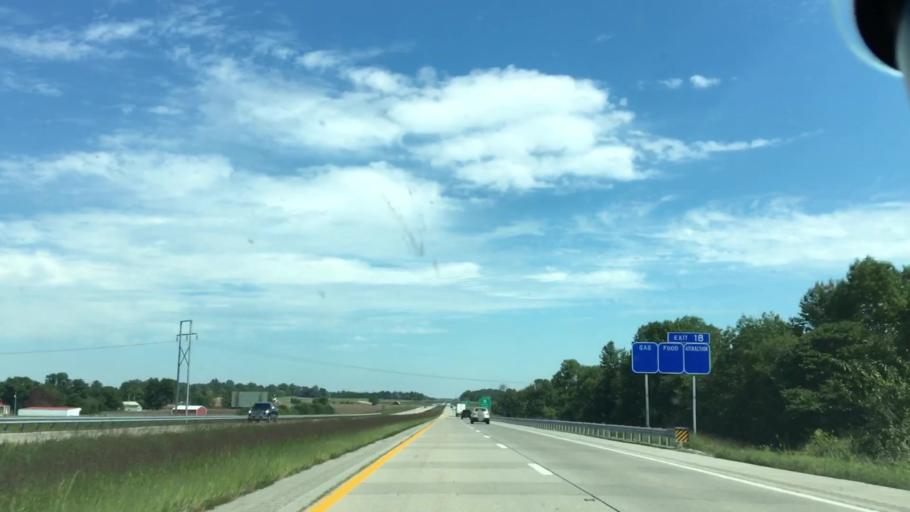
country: US
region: Kentucky
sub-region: Daviess County
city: Owensboro
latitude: 37.7532
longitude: -87.2756
